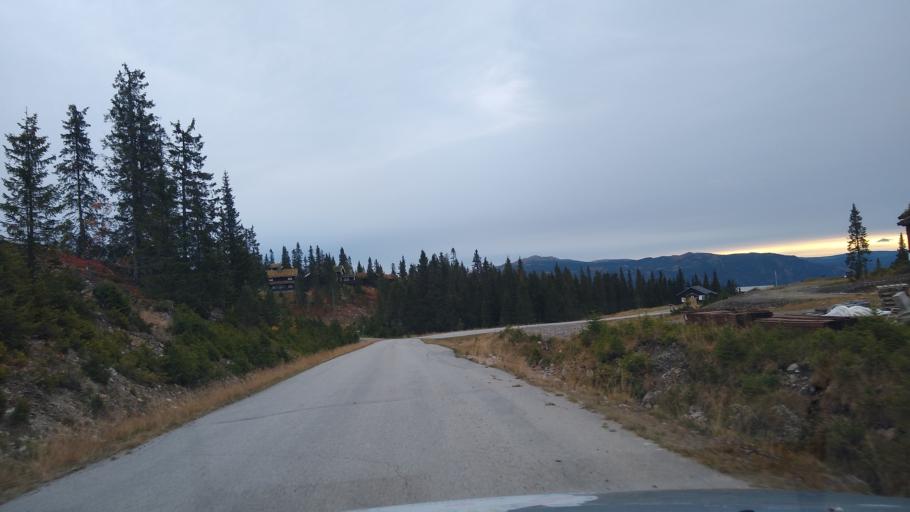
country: NO
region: Oppland
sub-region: Ringebu
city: Ringebu
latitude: 61.4736
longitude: 10.1317
